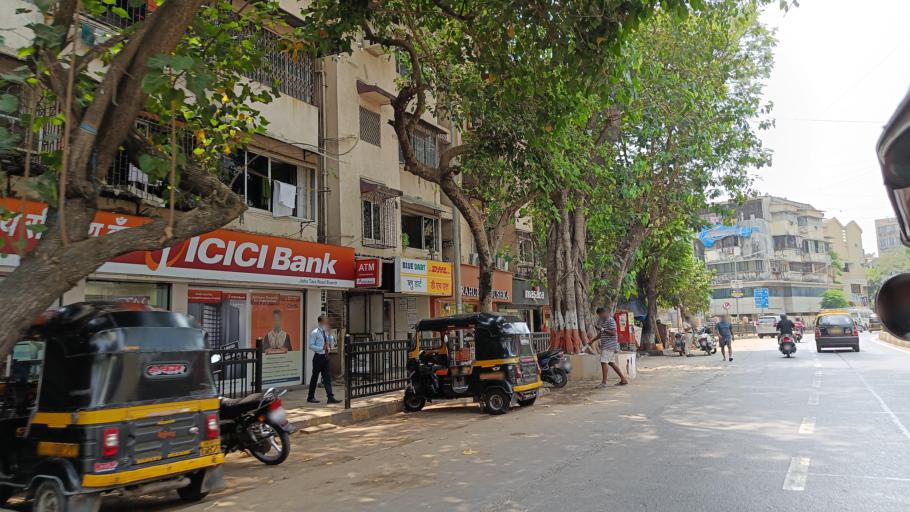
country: IN
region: Maharashtra
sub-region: Mumbai Suburban
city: Mumbai
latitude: 19.0878
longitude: 72.8272
